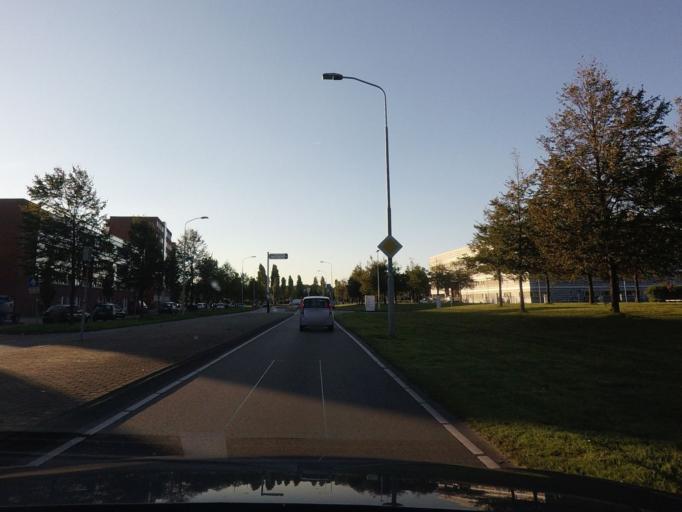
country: NL
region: North Holland
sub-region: Gemeente Bloemendaal
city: Bloemendaal
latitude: 52.4216
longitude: 4.6512
